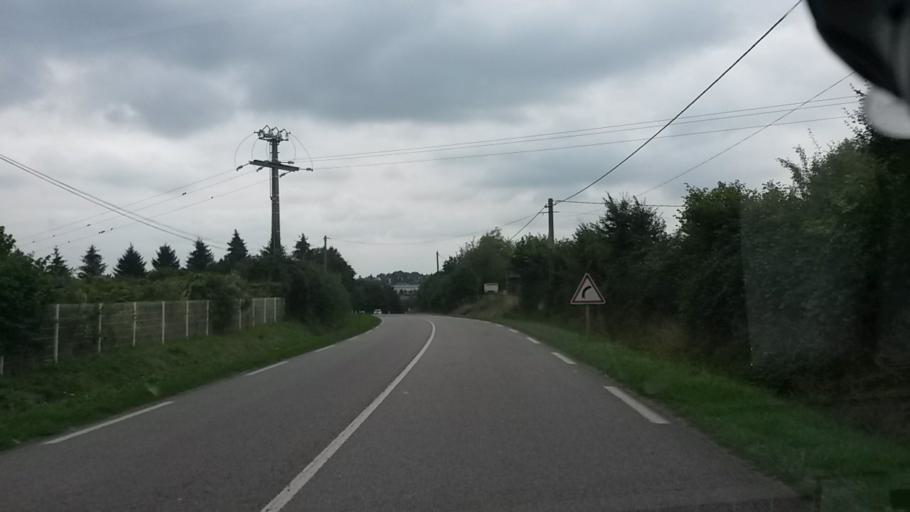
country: FR
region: Haute-Normandie
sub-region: Departement de la Seine-Maritime
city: Forges-les-Eaux
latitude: 49.6190
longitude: 1.5597
